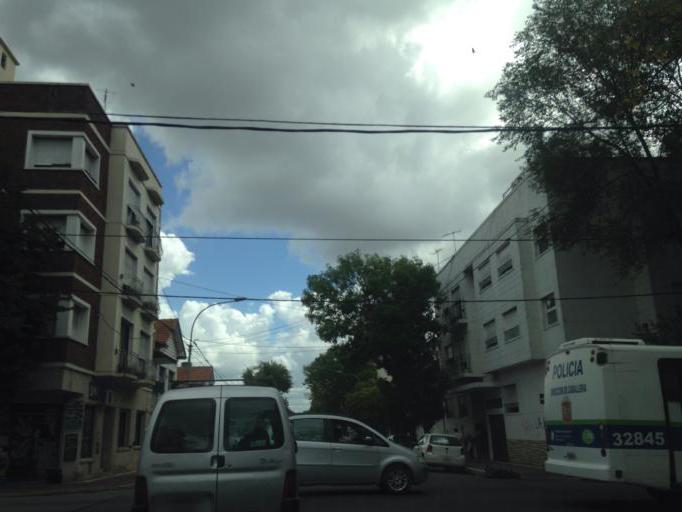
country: AR
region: Buenos Aires
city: Mar del Plata
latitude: -38.0076
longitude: -57.5532
